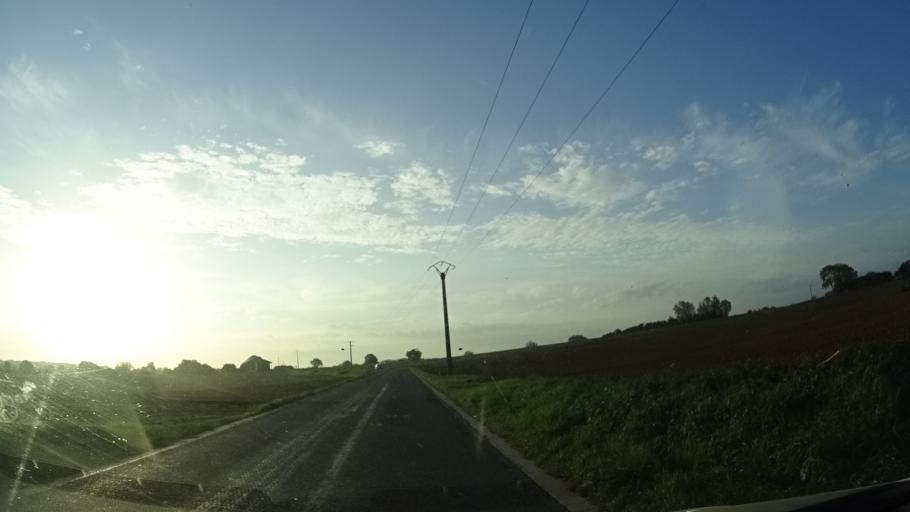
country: BE
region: Wallonia
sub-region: Province du Hainaut
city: Beaumont
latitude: 50.2664
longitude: 4.2214
